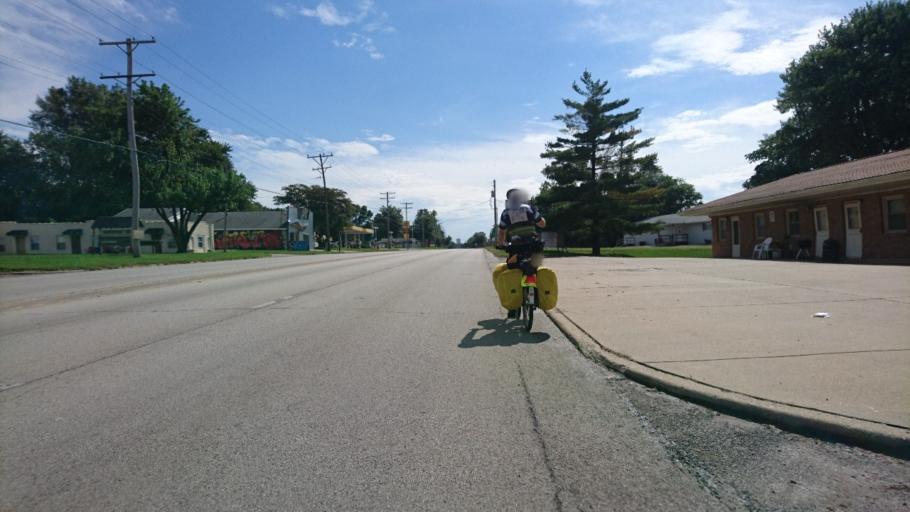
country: US
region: Illinois
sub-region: Sangamon County
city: Grandview
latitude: 39.8407
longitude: -89.6337
